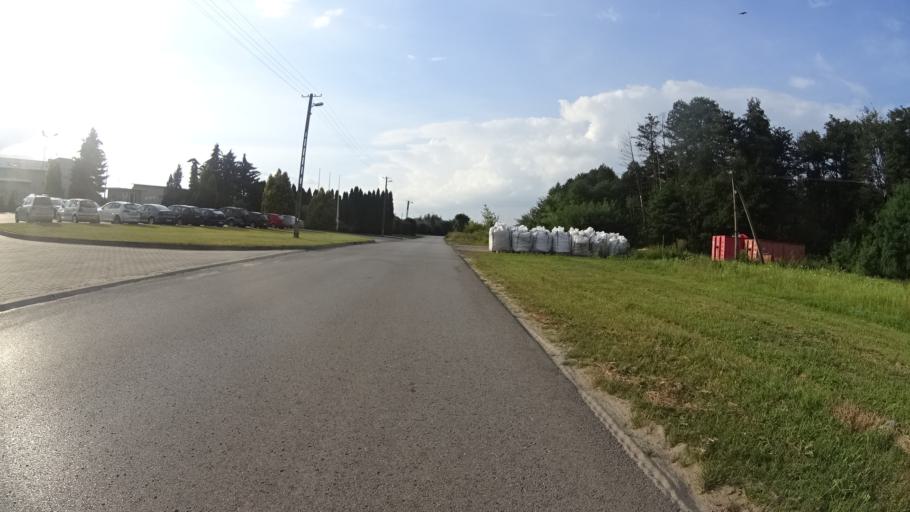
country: PL
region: Masovian Voivodeship
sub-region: Powiat grojecki
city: Mogielnica
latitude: 51.6777
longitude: 20.7350
